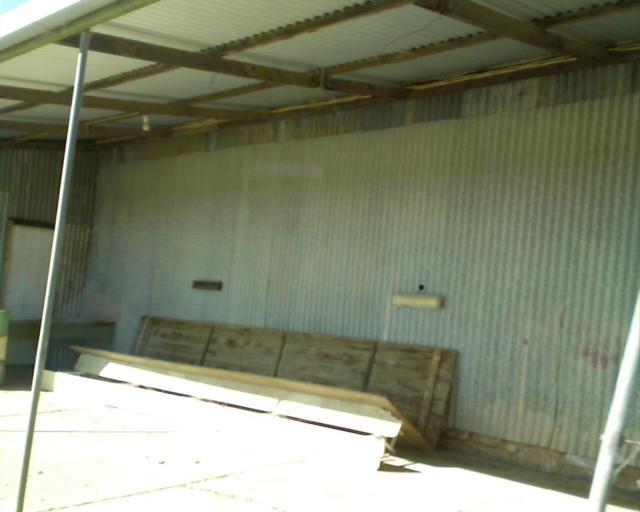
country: AU
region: South Australia
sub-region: Flinders Ranges
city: Quorn
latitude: -32.6491
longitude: 138.0932
